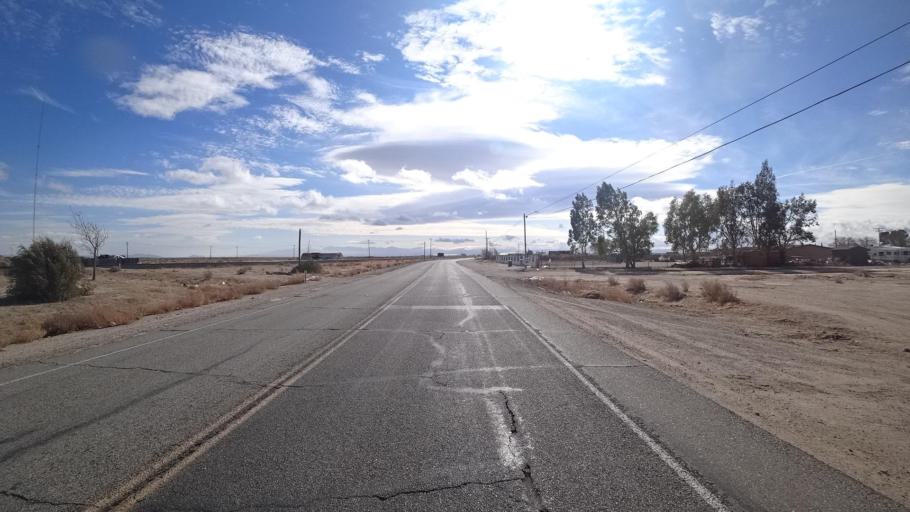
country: US
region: California
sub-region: Kern County
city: Rosamond
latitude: 34.8523
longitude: -118.1617
